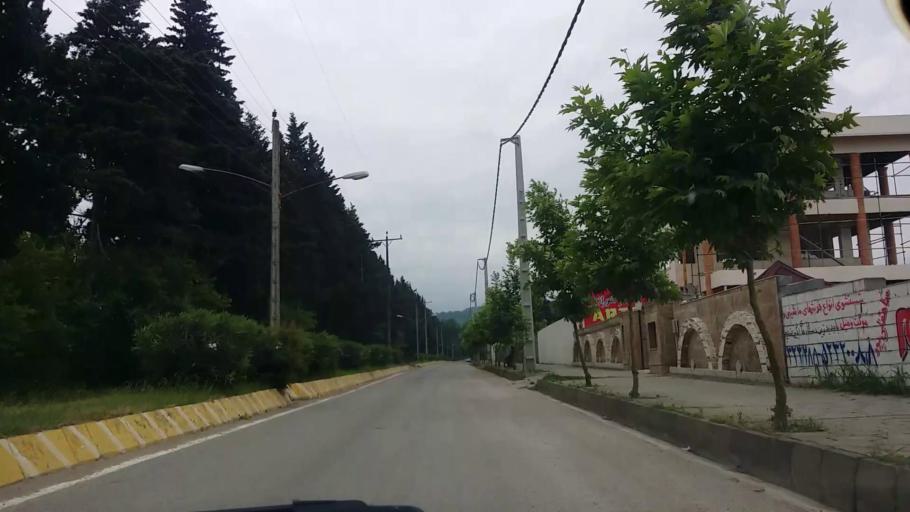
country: IR
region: Mazandaran
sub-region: Nowshahr
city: Nowshahr
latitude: 36.6362
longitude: 51.5024
